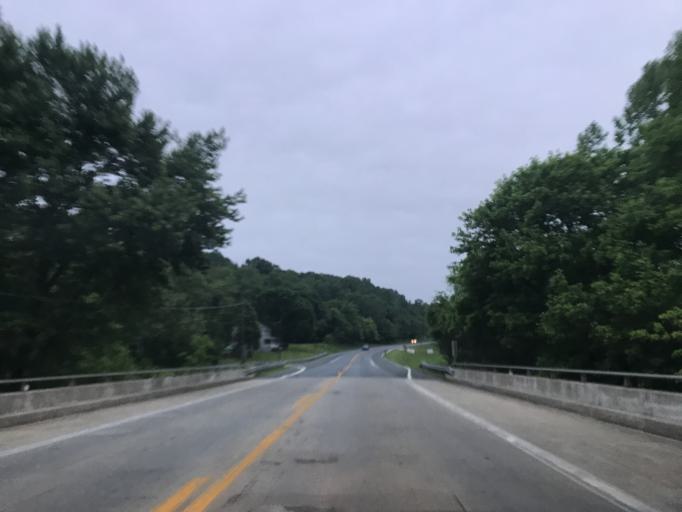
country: US
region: Maryland
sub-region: Frederick County
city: Linganore
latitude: 39.4479
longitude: -77.2483
